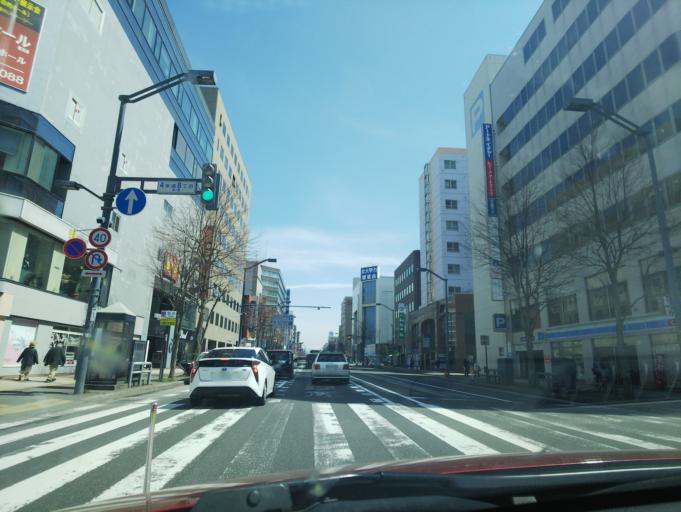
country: JP
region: Hokkaido
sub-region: Asahikawa-shi
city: Asahikawa
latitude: 43.7689
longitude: 142.3610
